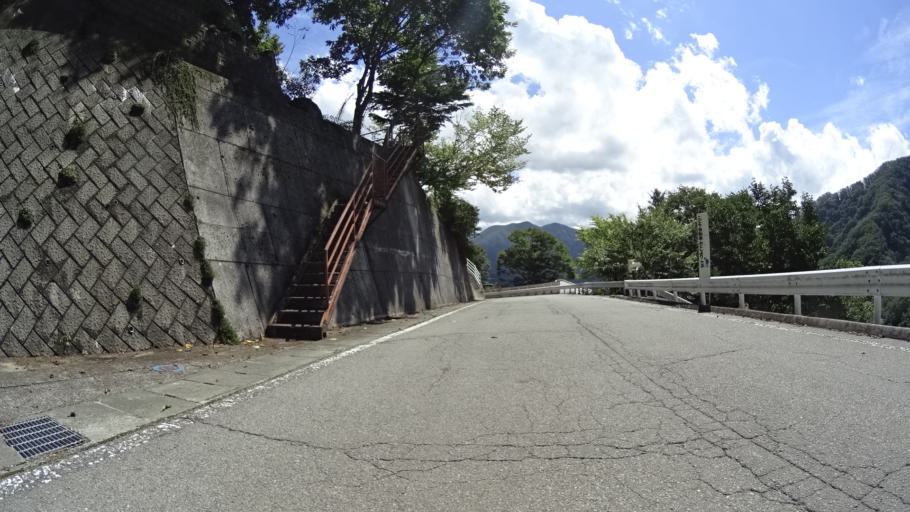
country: JP
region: Yamanashi
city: Enzan
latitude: 35.6598
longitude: 138.8112
